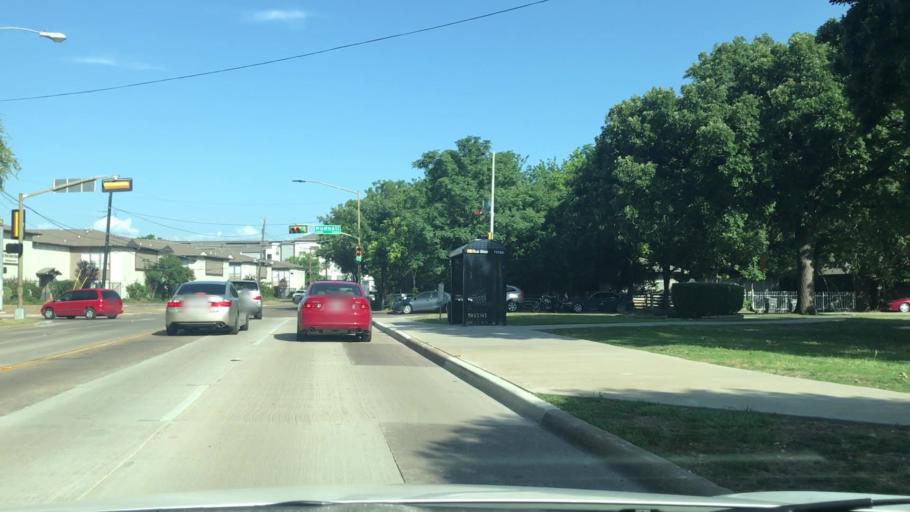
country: US
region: Texas
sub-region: Dallas County
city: Highland Park
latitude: 32.8231
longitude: -96.8279
